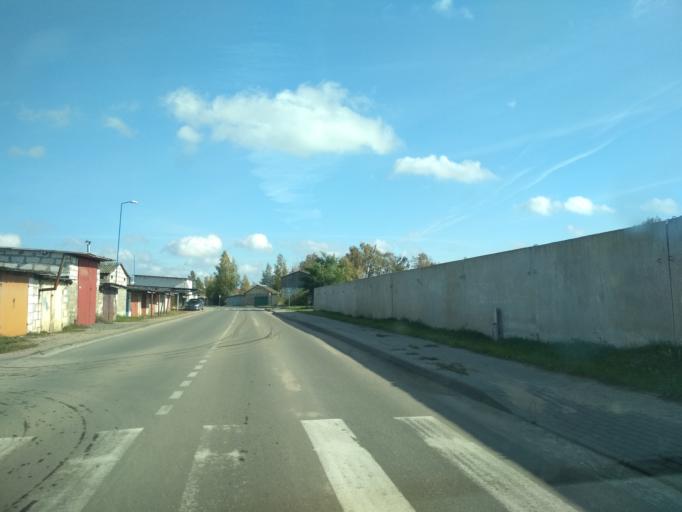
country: BY
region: Minsk
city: Mar''ina Horka
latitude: 53.5001
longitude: 28.1538
